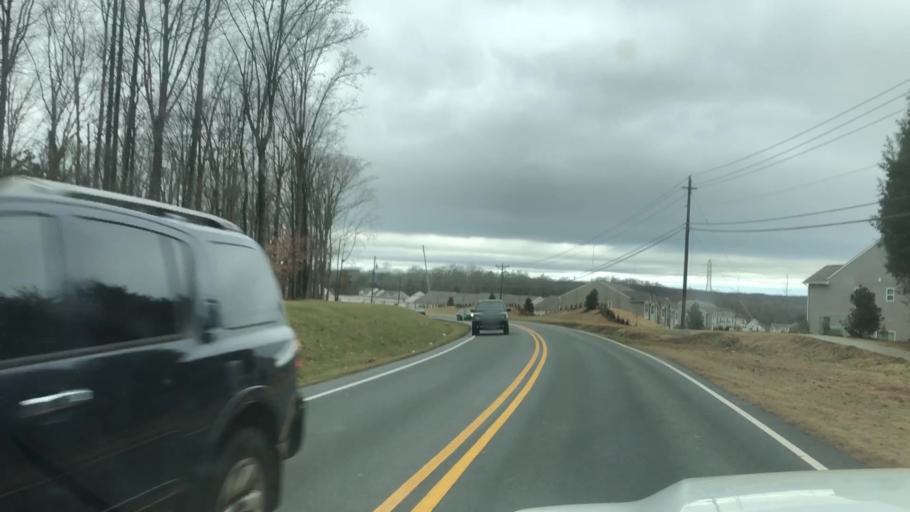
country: US
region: North Carolina
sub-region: Mecklenburg County
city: Mint Hill
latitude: 35.2421
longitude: -80.6766
